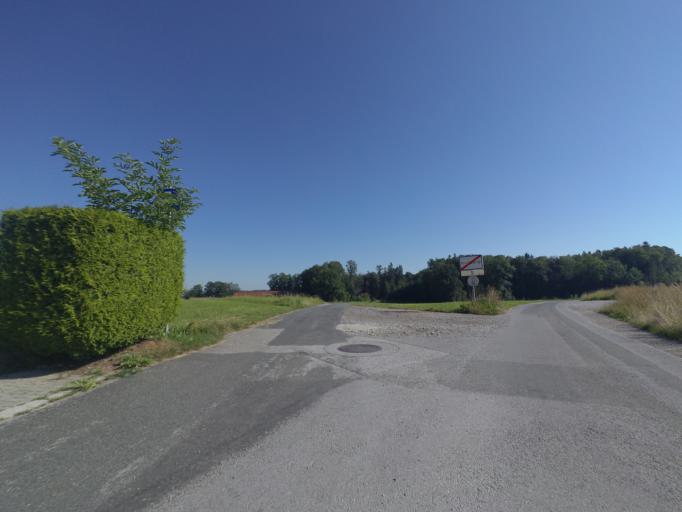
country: AT
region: Salzburg
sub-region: Politischer Bezirk Salzburg-Umgebung
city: Hallwang
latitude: 47.8533
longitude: 13.0865
